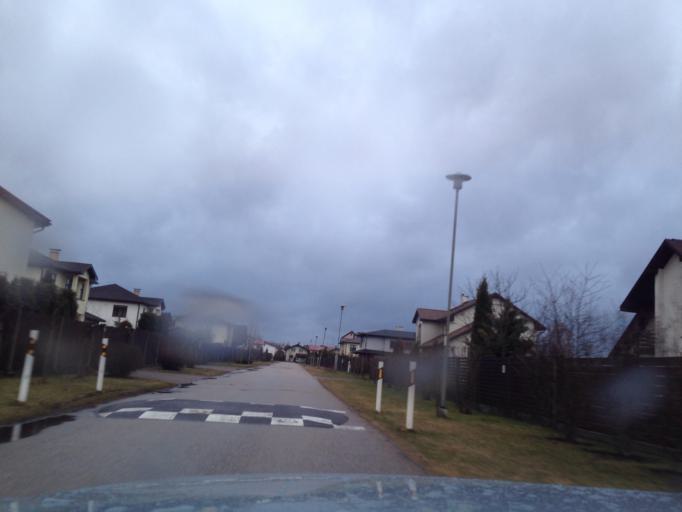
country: LV
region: Marupe
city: Marupe
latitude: 56.8890
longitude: 24.0320
